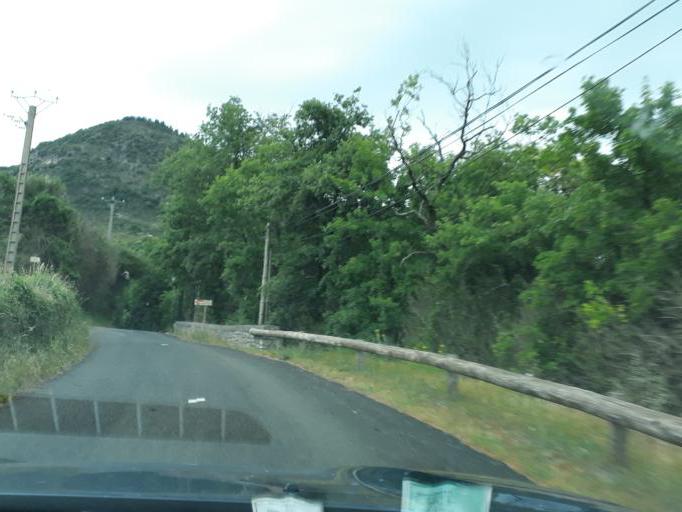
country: FR
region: Languedoc-Roussillon
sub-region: Departement de l'Herault
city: Lodeve
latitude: 43.7768
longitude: 3.2916
